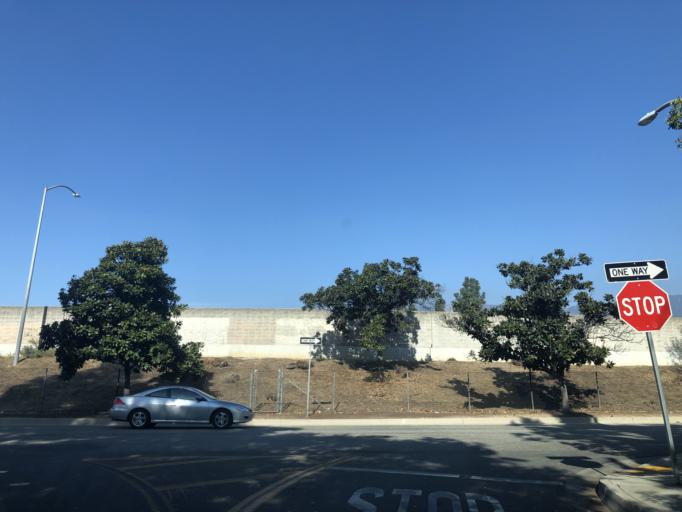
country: US
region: California
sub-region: Los Angeles County
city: Pasadena
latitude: 34.1514
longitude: -118.1244
